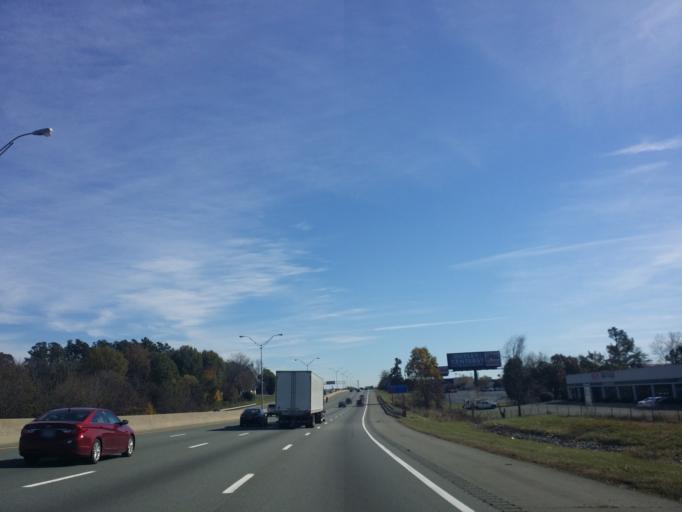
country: US
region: North Carolina
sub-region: Alamance County
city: Elon
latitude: 36.0687
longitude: -79.4807
